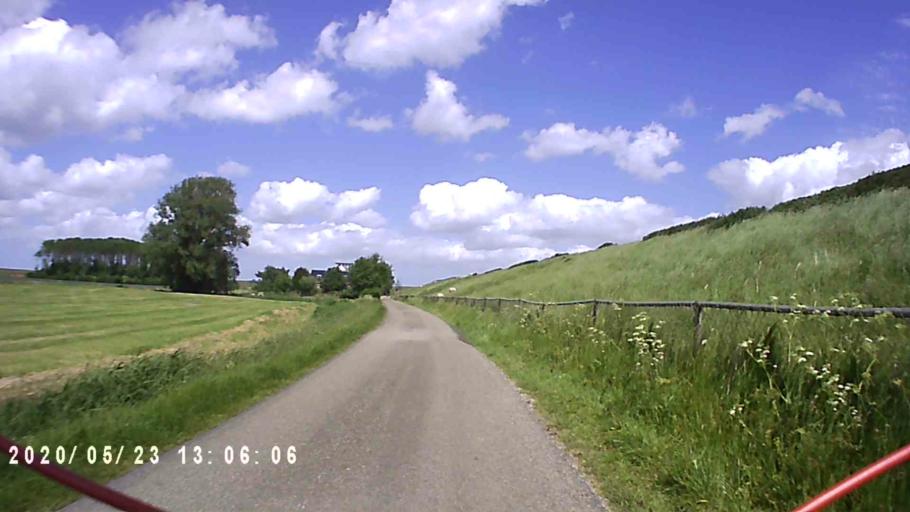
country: DE
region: Lower Saxony
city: Emden
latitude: 53.2958
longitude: 7.0753
